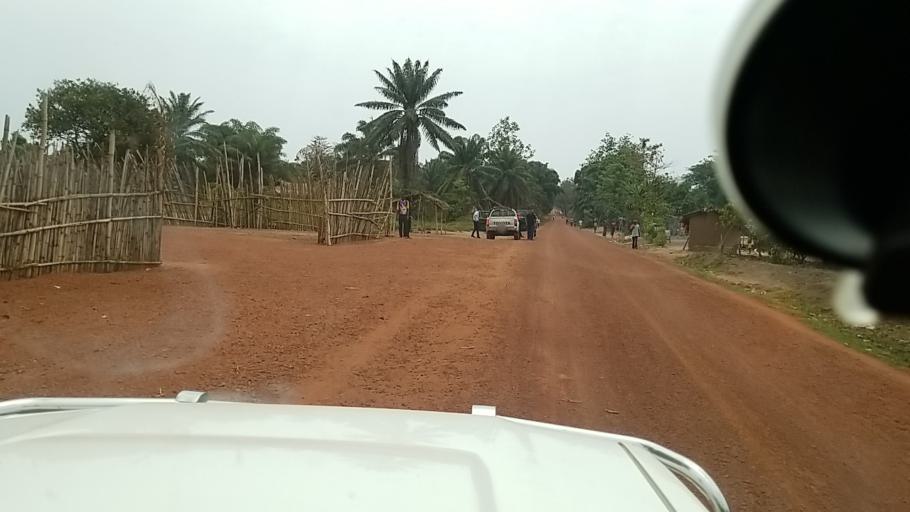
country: CD
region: Equateur
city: Libenge
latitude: 3.7217
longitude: 18.7705
